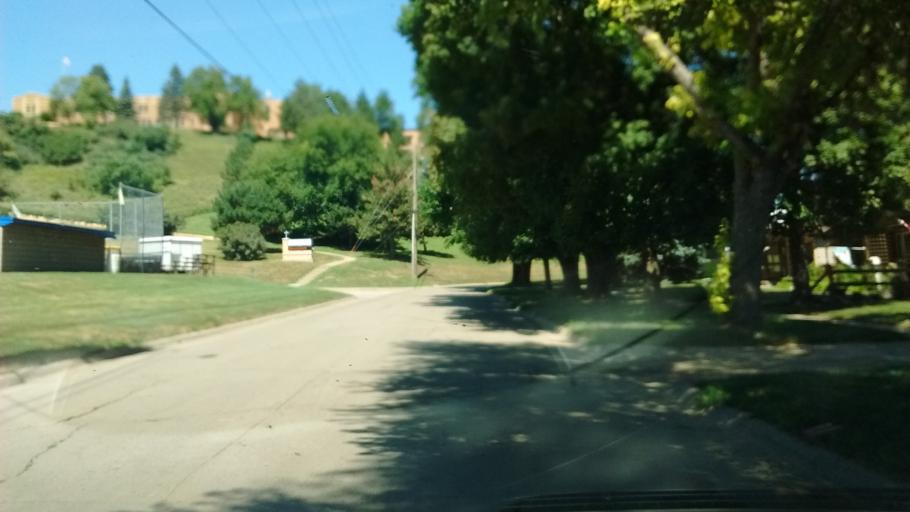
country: US
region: Iowa
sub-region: Woodbury County
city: Sioux City
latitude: 42.5247
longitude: -96.4256
